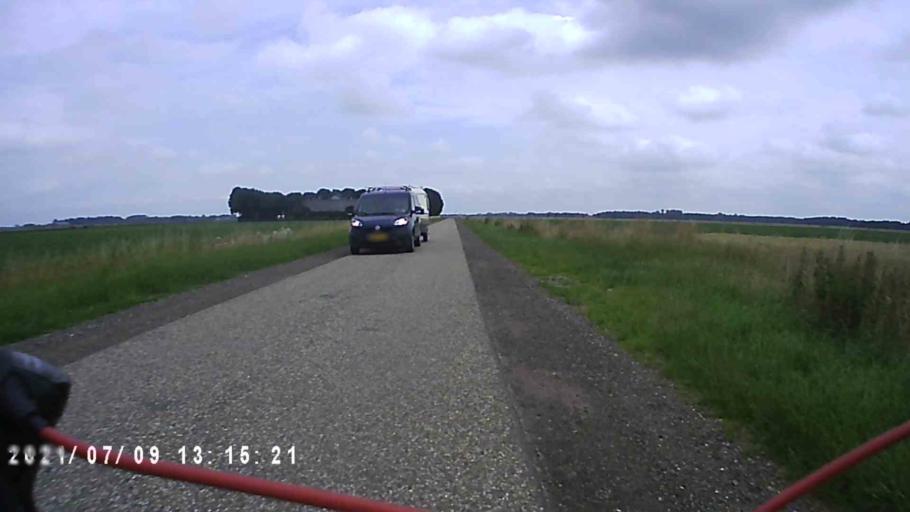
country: NL
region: Groningen
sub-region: Gemeente Vlagtwedde
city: Vlagtwedde
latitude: 53.1188
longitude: 7.1417
